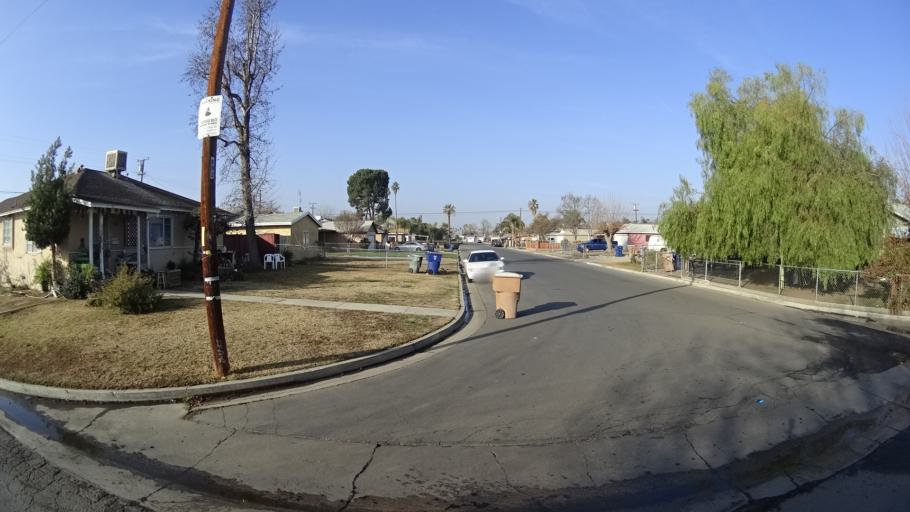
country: US
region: California
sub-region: Kern County
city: Bakersfield
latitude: 35.3362
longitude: -119.0227
